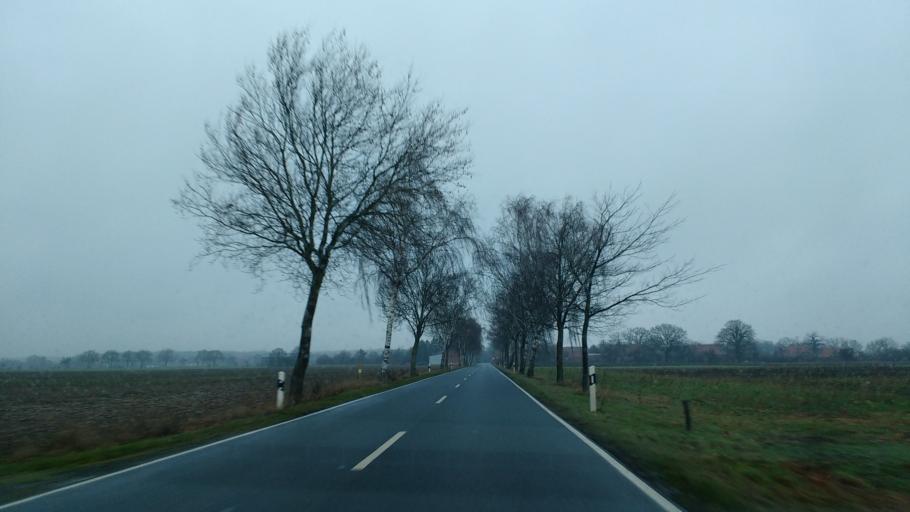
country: DE
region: Lower Saxony
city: Gilten
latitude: 52.6588
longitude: 9.5738
